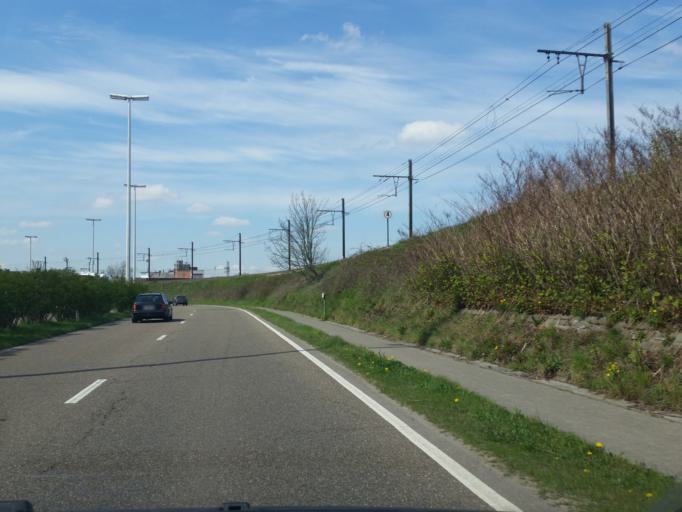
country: BE
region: Flanders
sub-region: Provincie Oost-Vlaanderen
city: Sint-Niklaas
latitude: 51.1728
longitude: 4.1568
